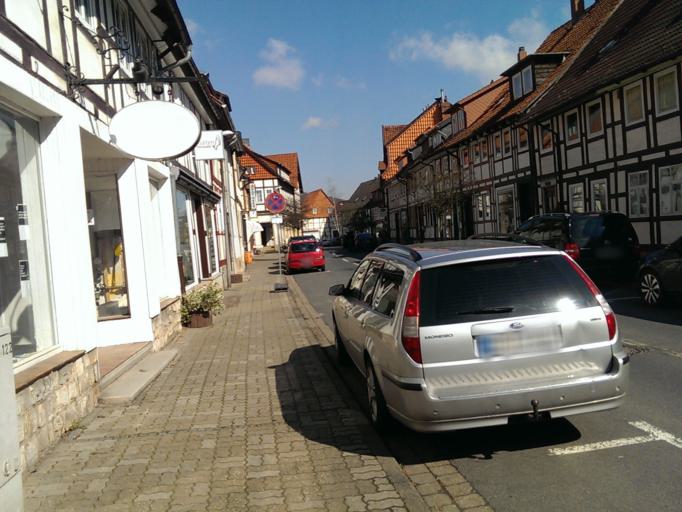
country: DE
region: Lower Saxony
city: Bad Salzdetfurth
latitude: 52.0616
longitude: 10.0073
